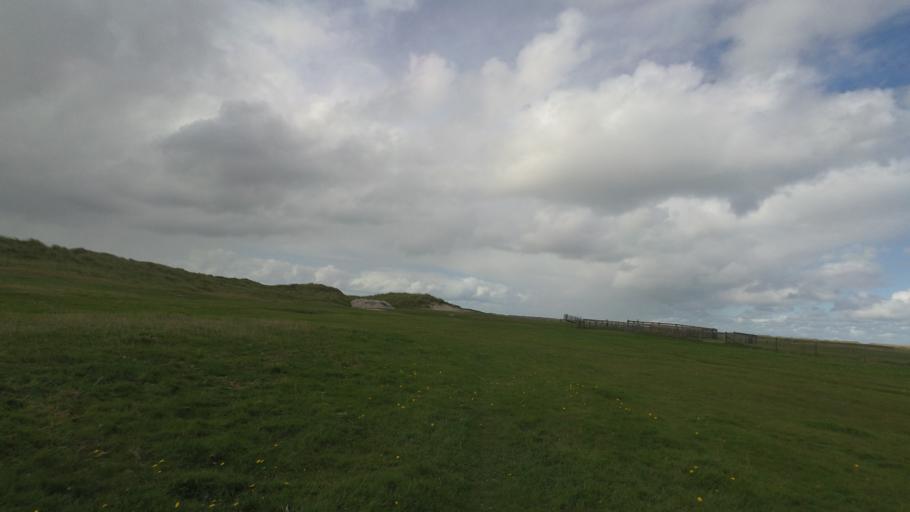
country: NL
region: Friesland
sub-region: Gemeente Ameland
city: Nes
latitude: 53.4502
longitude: 5.8605
